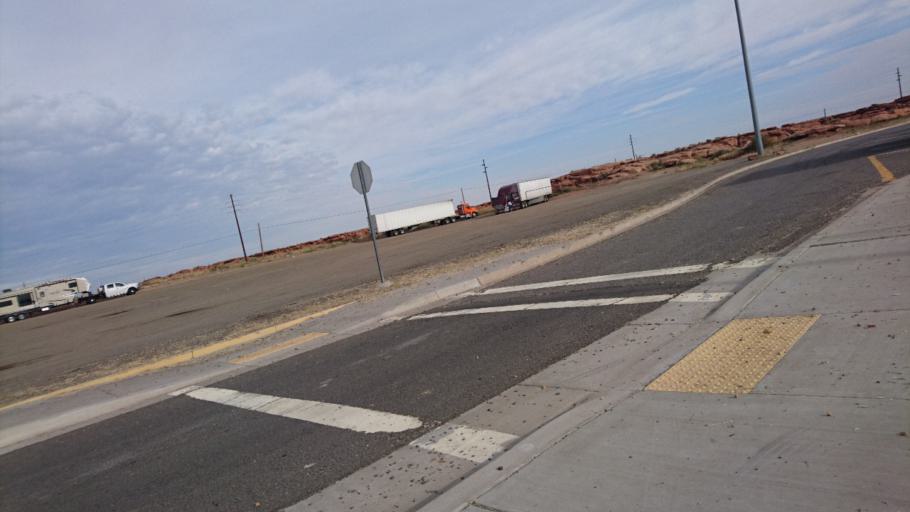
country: US
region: Arizona
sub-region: Coconino County
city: LeChee
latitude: 35.1038
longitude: -110.9940
